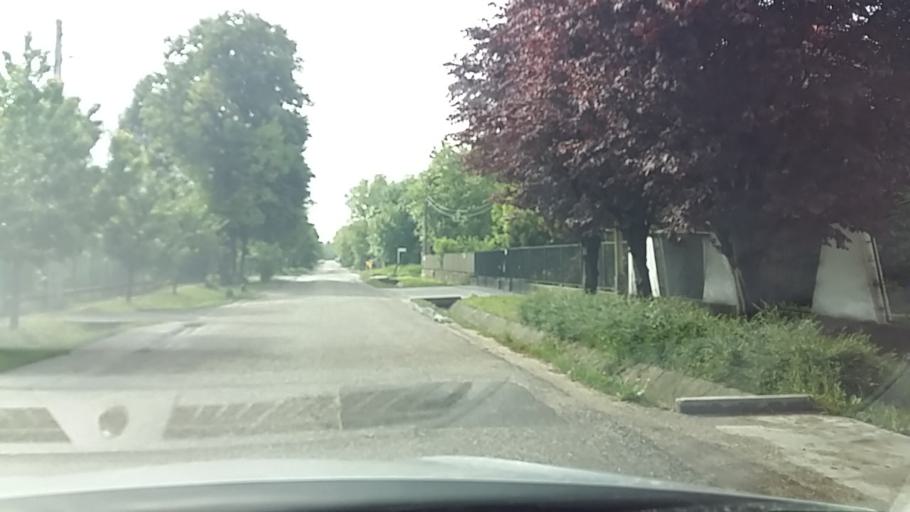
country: HU
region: Budapest
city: Budapest XVI. keruelet
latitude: 47.5041
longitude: 19.2073
